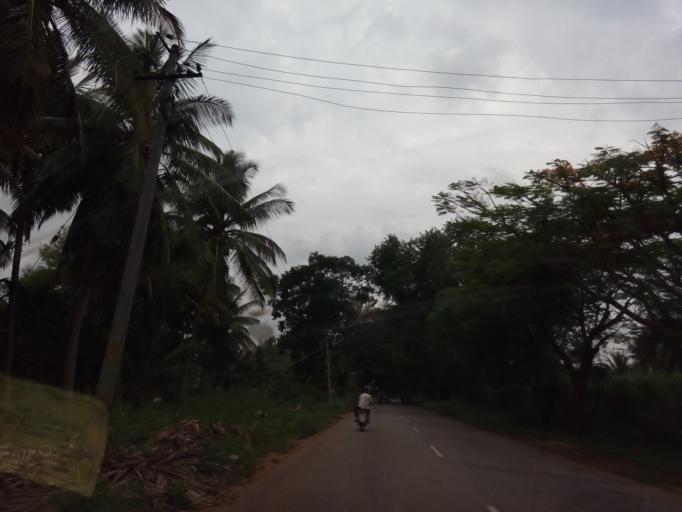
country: IN
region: Karnataka
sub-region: Hassan
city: Channarayapatna
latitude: 12.8757
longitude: 76.4343
